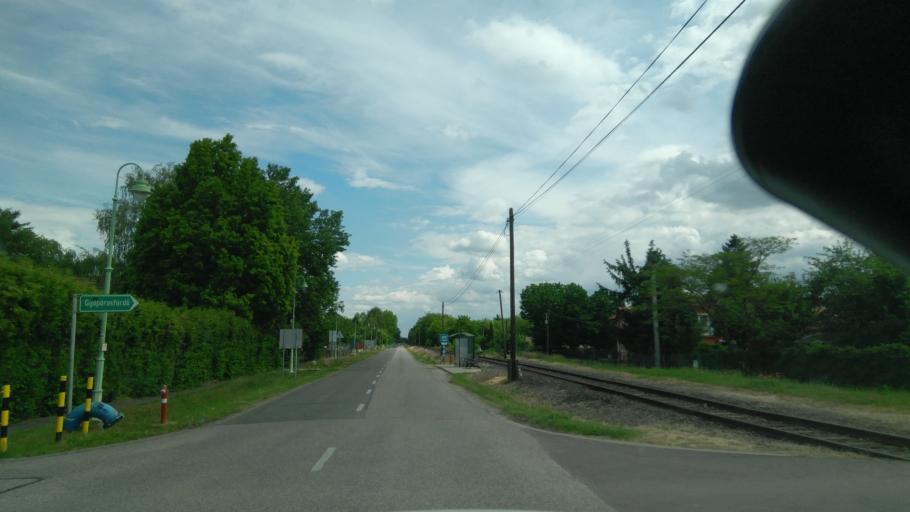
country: HU
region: Bekes
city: Oroshaza
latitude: 46.5677
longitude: 20.6309
